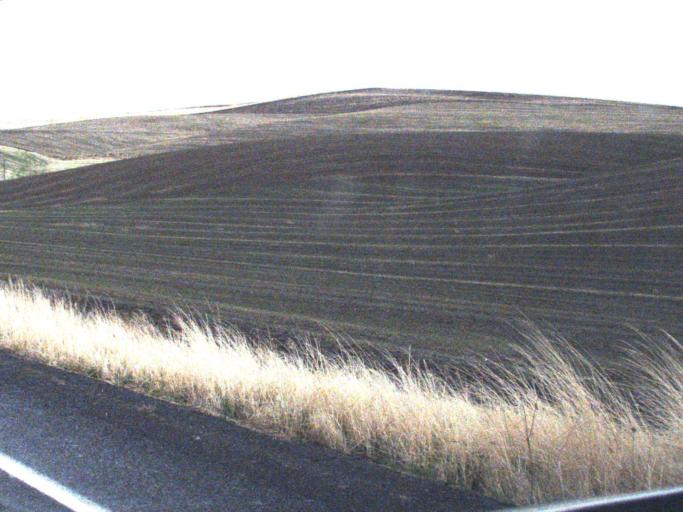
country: US
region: Washington
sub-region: Walla Walla County
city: Waitsburg
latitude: 46.1825
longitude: -118.1367
